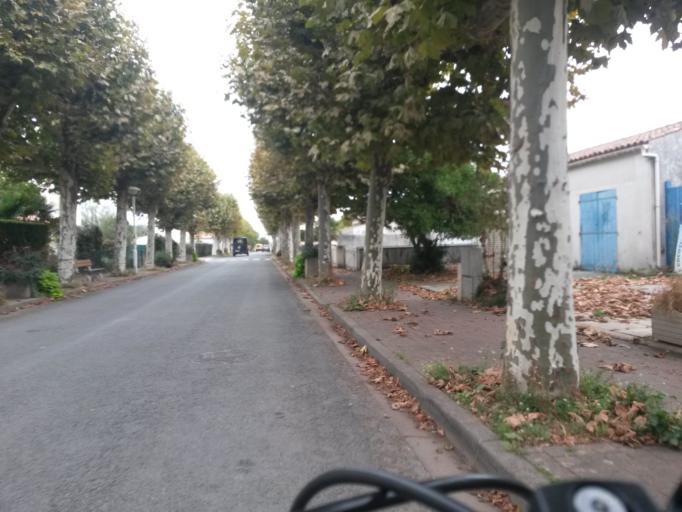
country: FR
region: Poitou-Charentes
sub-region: Departement de la Charente-Maritime
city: Saint-Denis-d'Oleron
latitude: 46.0350
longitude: -1.3746
